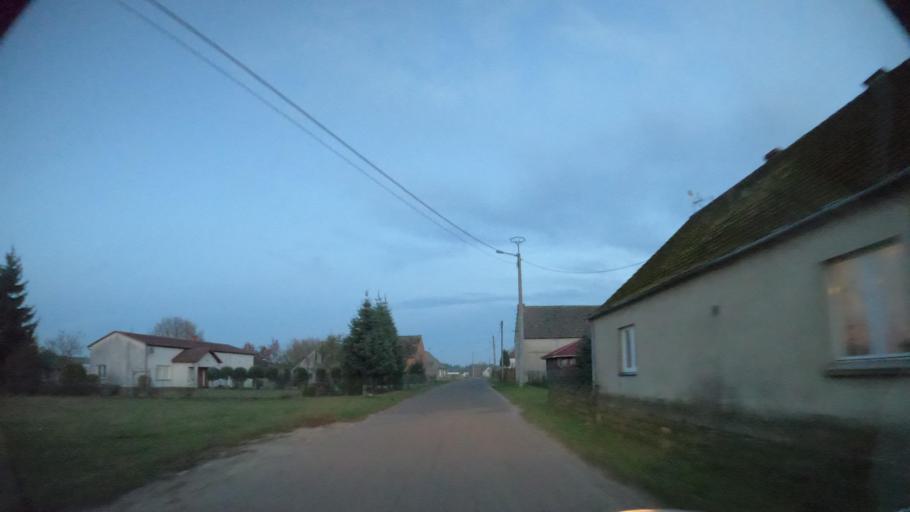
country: PL
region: Greater Poland Voivodeship
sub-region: Powiat zlotowski
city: Sypniewo
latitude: 53.4333
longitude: 16.6907
